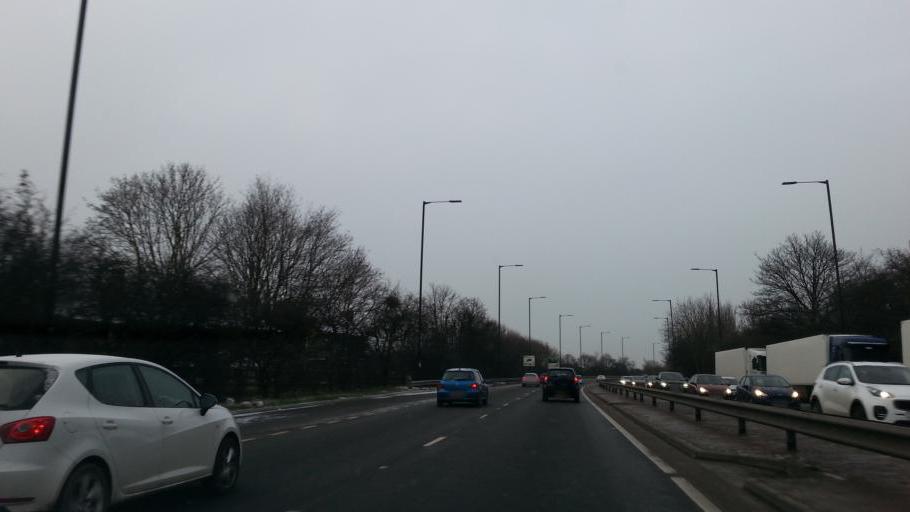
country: GB
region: England
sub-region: Rotherham
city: Orgreave
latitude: 53.3823
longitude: -1.3916
